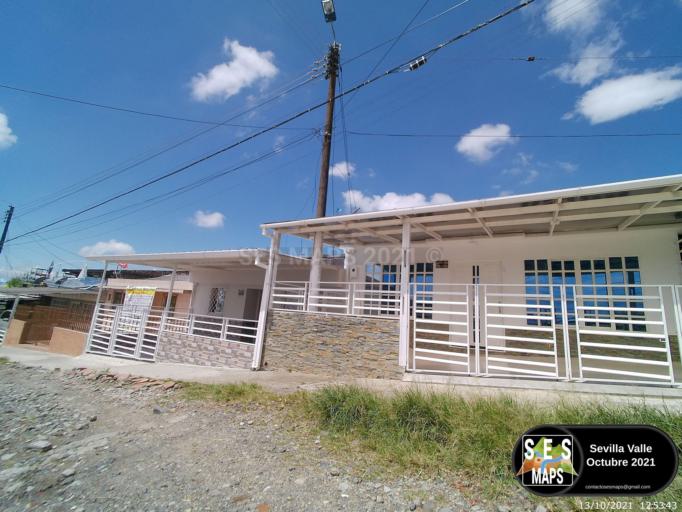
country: CO
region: Valle del Cauca
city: Sevilla
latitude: 4.2710
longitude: -75.9299
